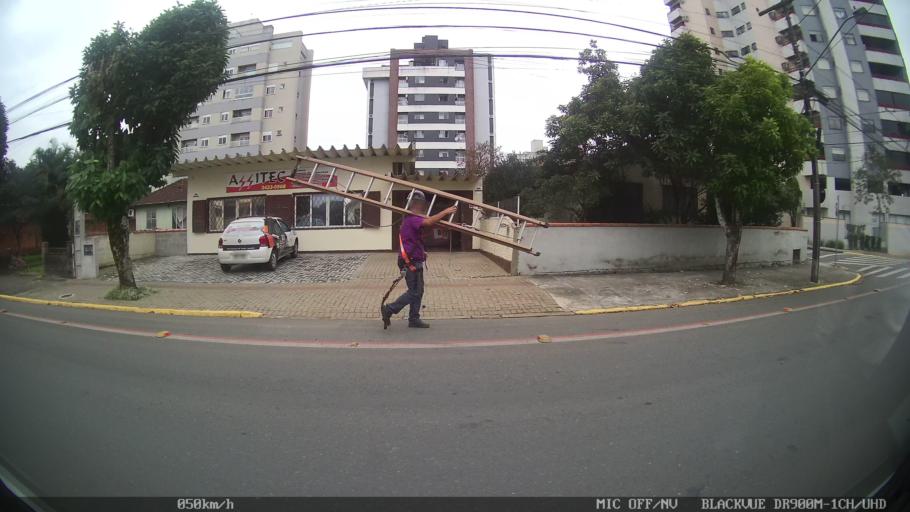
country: BR
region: Santa Catarina
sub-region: Joinville
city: Joinville
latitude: -26.2864
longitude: -48.8451
